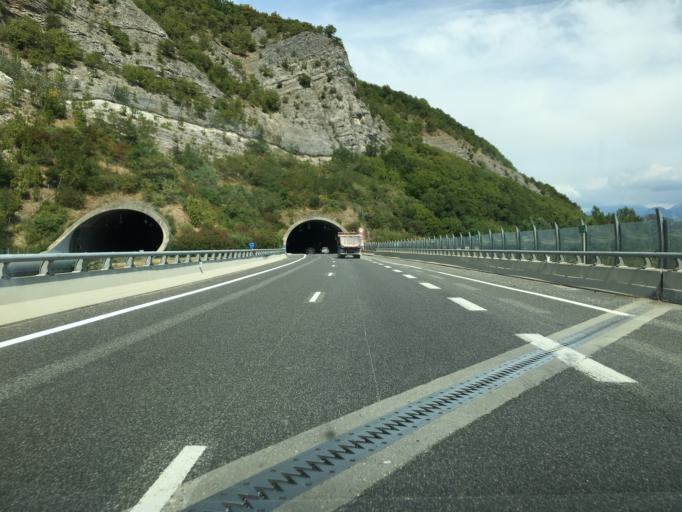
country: FR
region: Rhone-Alpes
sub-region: Departement de l'Isere
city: Allieres-et-Risset
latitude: 45.0797
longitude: 5.6795
